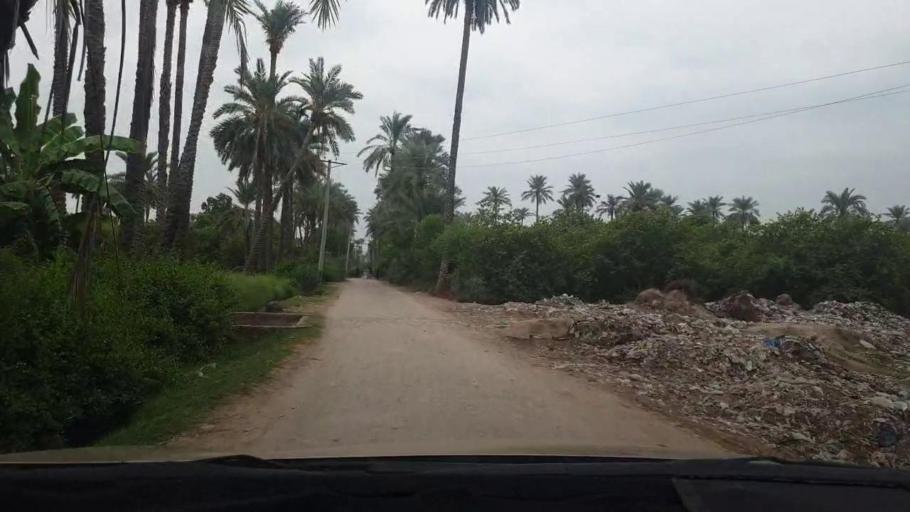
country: PK
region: Sindh
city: Larkana
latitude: 27.5617
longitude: 68.2311
